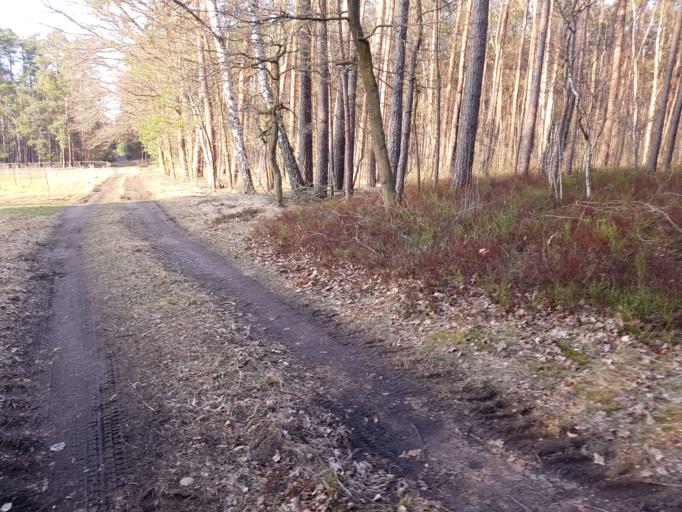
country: DE
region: Brandenburg
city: Schonewalde
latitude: 51.6339
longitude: 13.6160
